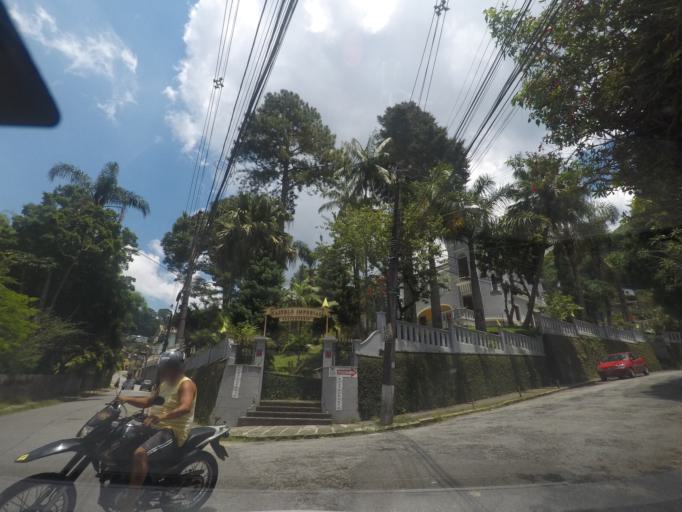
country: BR
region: Rio de Janeiro
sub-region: Petropolis
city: Petropolis
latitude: -22.5018
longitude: -43.1852
